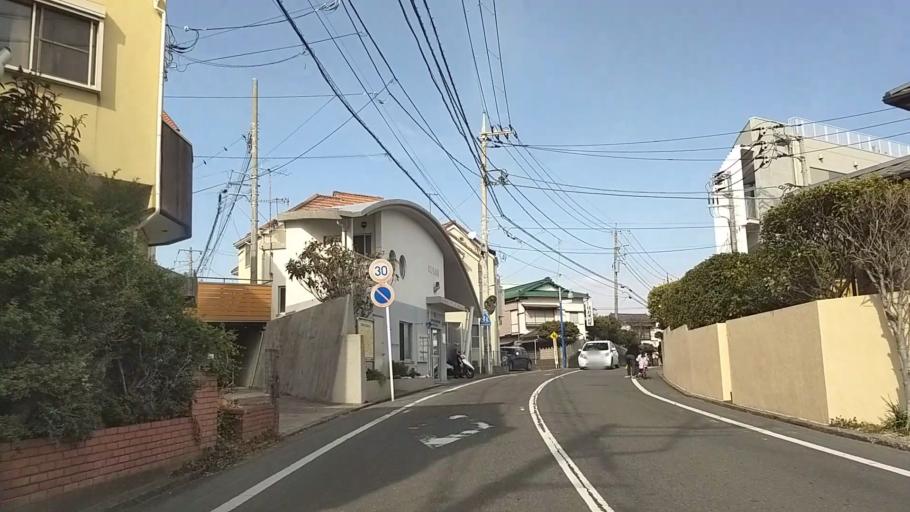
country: JP
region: Kanagawa
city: Chigasaki
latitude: 35.3260
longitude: 139.4026
